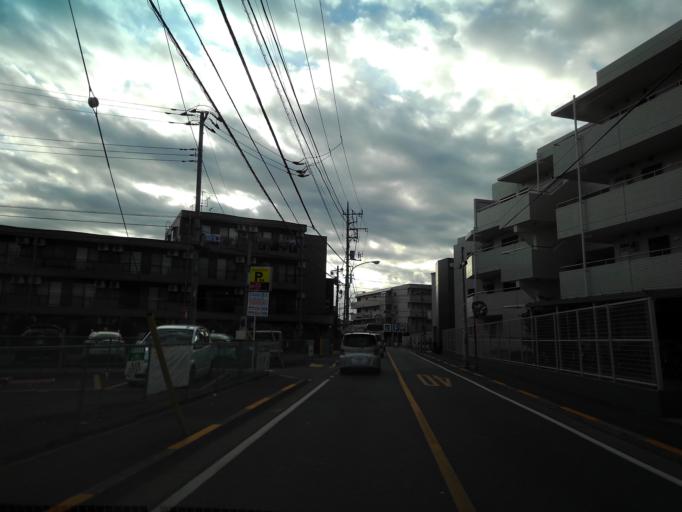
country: JP
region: Tokyo
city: Mitaka-shi
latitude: 35.6788
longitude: 139.5732
